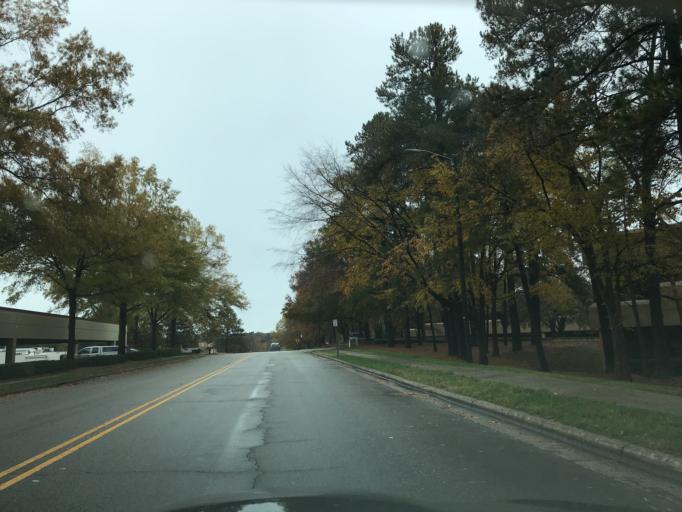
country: US
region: North Carolina
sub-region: Wake County
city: Raleigh
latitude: 35.8423
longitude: -78.6145
